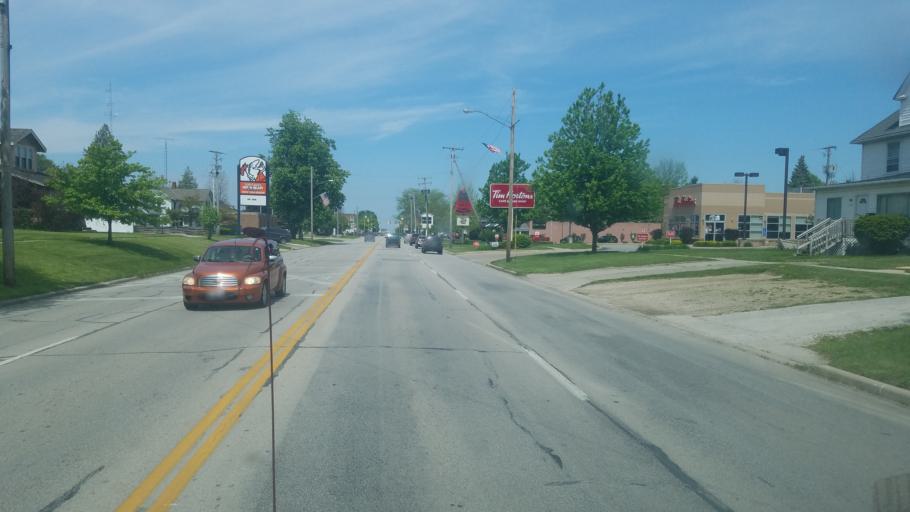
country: US
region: Ohio
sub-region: Sandusky County
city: Fremont
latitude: 41.3513
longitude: -83.1231
